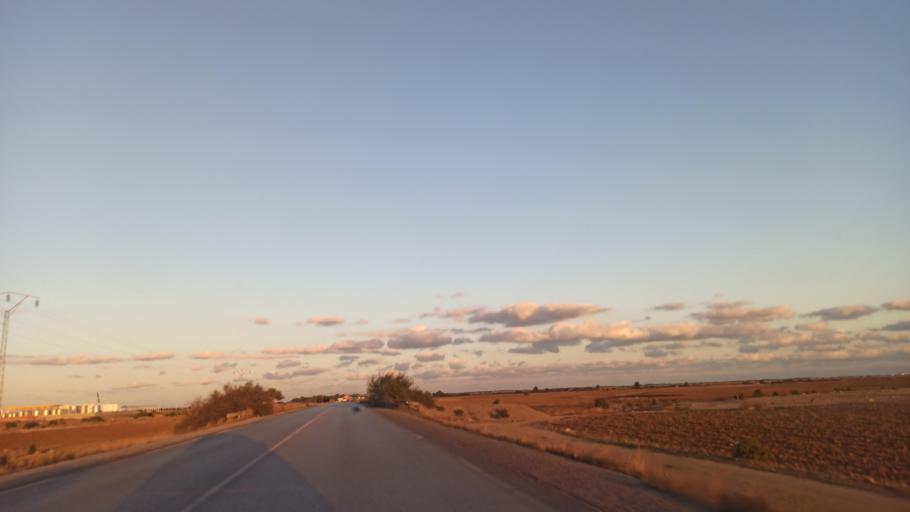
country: TN
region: Susah
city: Harqalah
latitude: 36.1028
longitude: 10.3913
